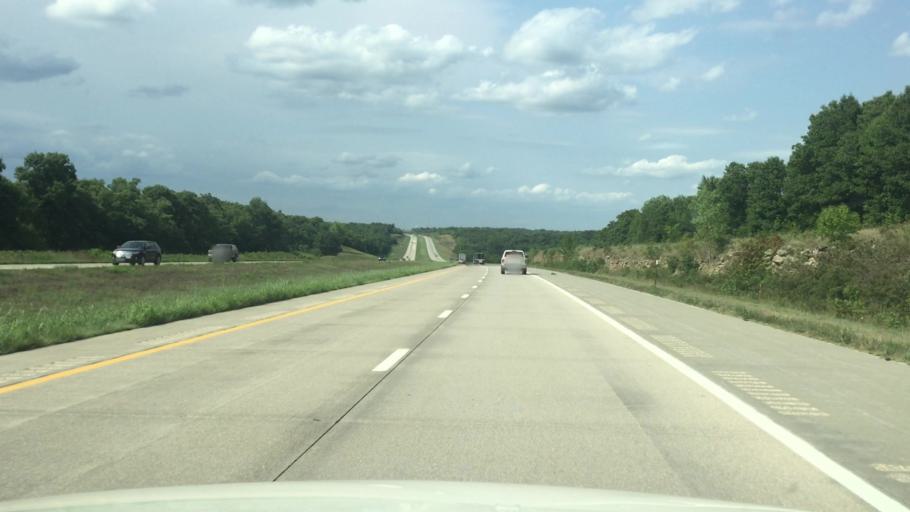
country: US
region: Kansas
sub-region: Miami County
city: Louisburg
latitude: 38.5877
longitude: -94.6942
